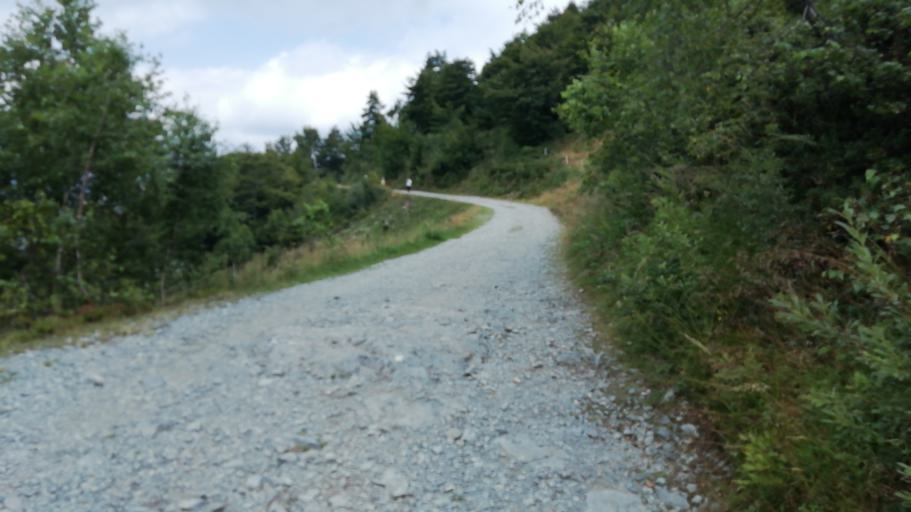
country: IT
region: Piedmont
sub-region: Provincia di Biella
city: Camandona
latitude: 45.6666
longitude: 8.0732
